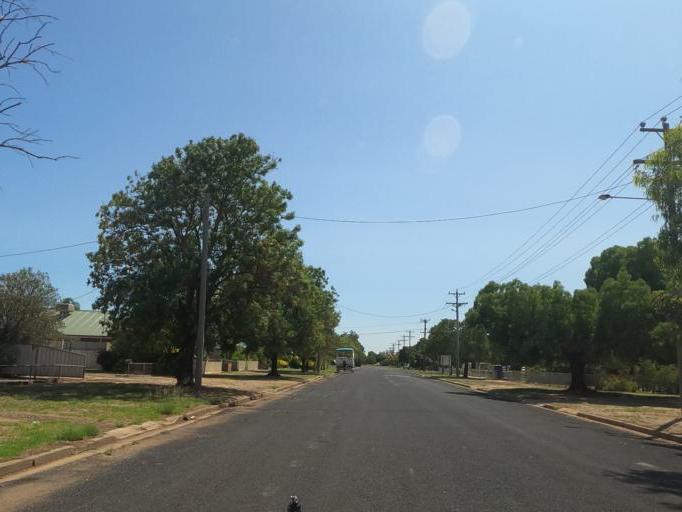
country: AU
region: New South Wales
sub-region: Corowa Shire
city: Mulwala
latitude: -35.9866
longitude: 146.0061
